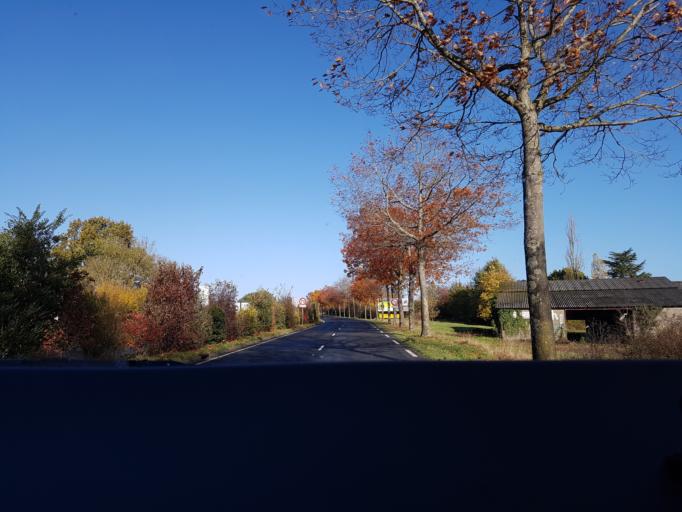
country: FR
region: Pays de la Loire
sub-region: Departement de Maine-et-Loire
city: Cholet
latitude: 47.0628
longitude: -0.9052
